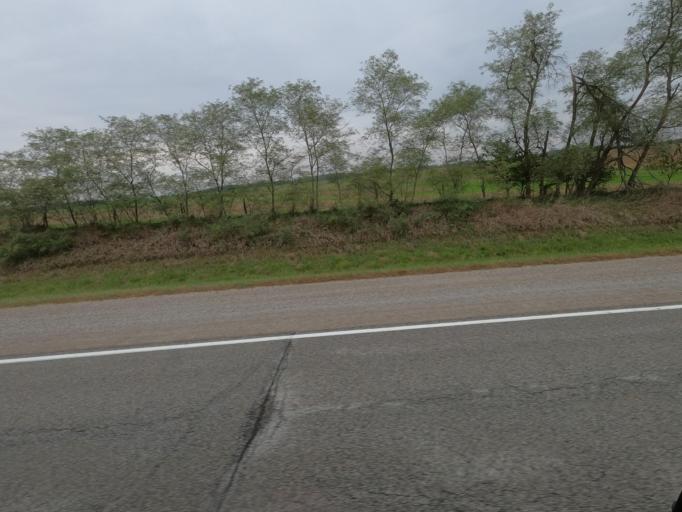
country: US
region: Iowa
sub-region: Van Buren County
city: Keosauqua
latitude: 40.8431
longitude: -92.0170
